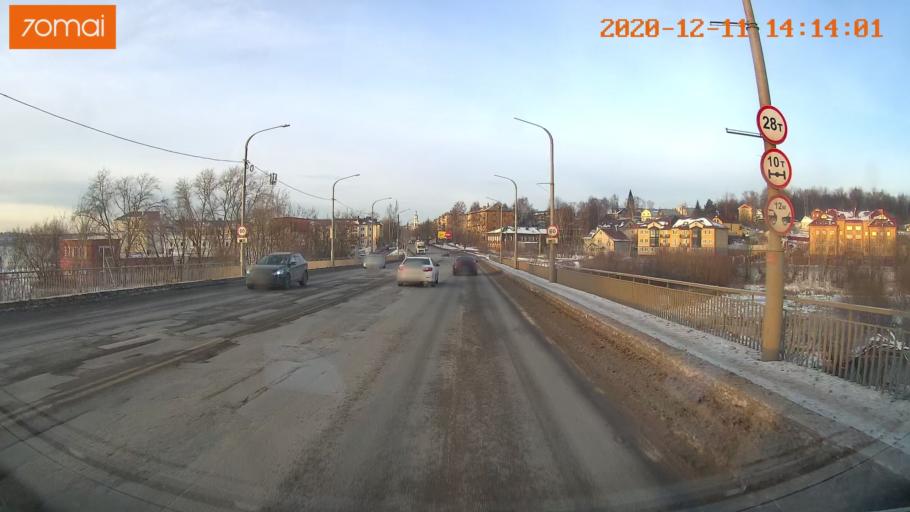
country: RU
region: Kostroma
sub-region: Kostromskoy Rayon
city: Kostroma
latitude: 57.7496
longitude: 40.9547
